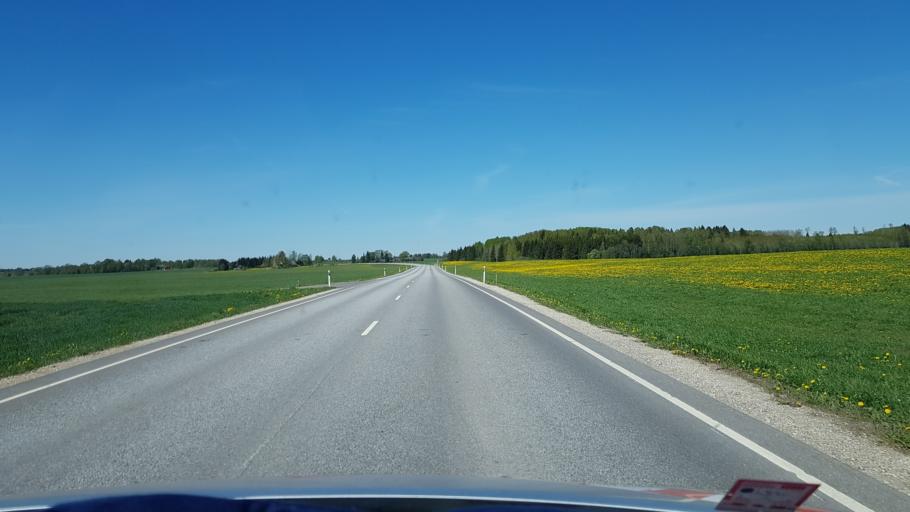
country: EE
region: Tartu
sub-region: Tartu linn
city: Tartu
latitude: 58.3870
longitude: 26.6058
